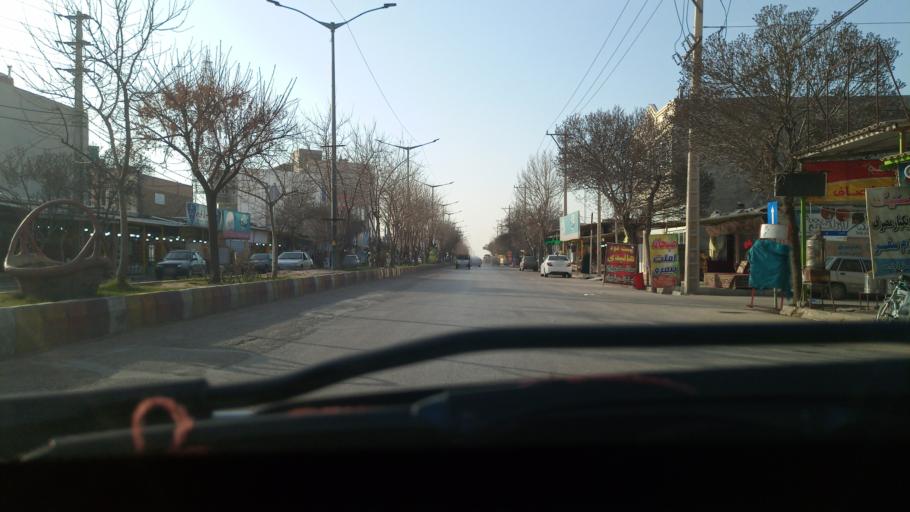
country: IR
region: Khorasan-e Shomali
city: Faruj
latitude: 37.2327
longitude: 58.2188
